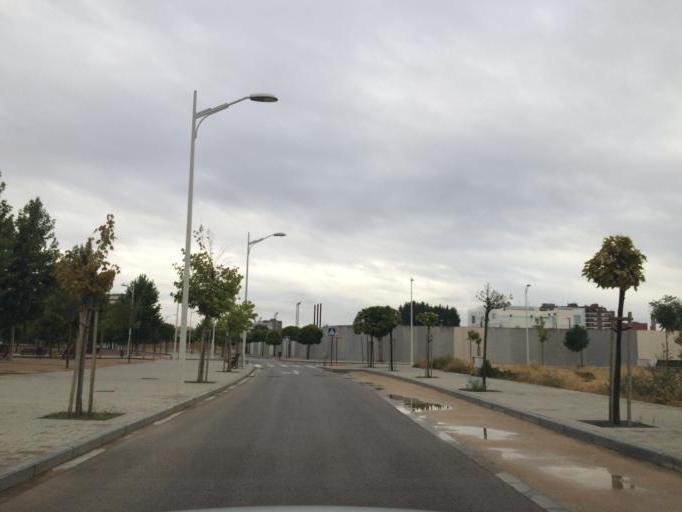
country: ES
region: Castille-La Mancha
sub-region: Provincia de Albacete
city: Albacete
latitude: 39.0084
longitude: -1.8599
